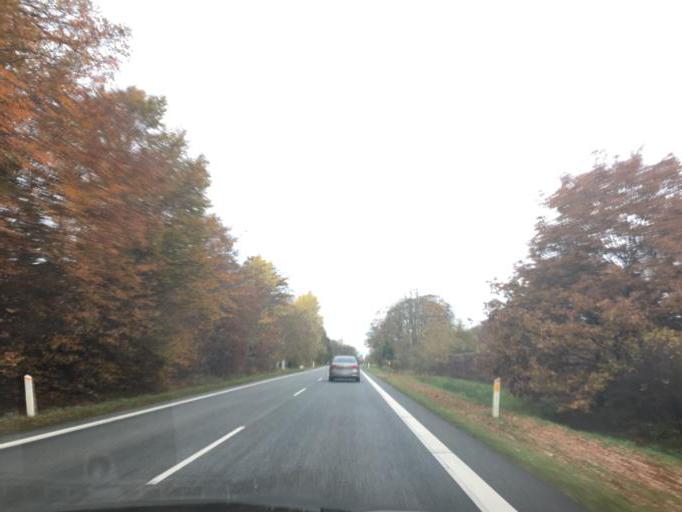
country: DK
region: South Denmark
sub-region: Vejle Kommune
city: Vejle
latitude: 55.6207
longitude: 9.4948
